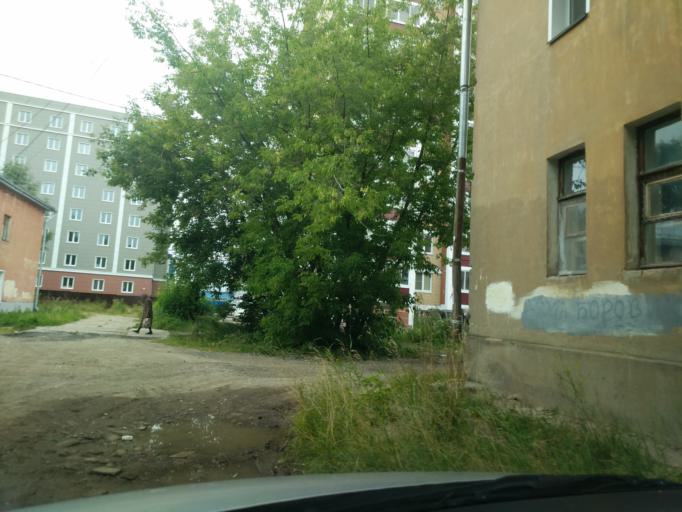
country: RU
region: Kirov
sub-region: Kirovo-Chepetskiy Rayon
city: Kirov
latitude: 58.6366
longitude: 49.6210
